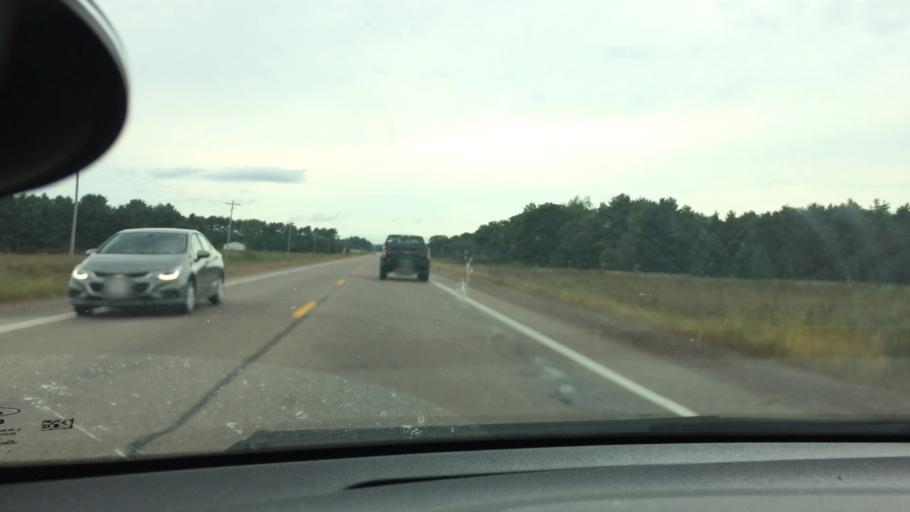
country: US
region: Wisconsin
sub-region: Trempealeau County
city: Osseo
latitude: 44.5872
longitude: -91.1505
